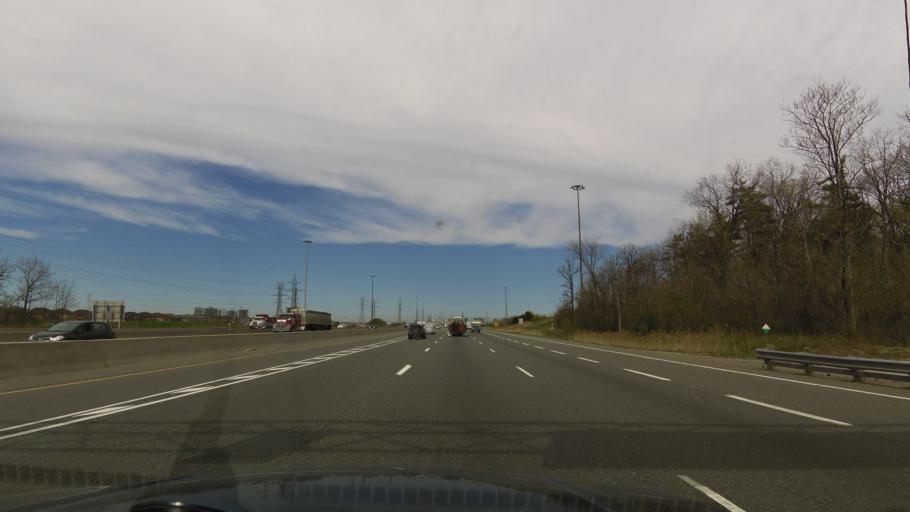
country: CA
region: Ontario
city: Mississauga
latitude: 43.5369
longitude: -79.7166
